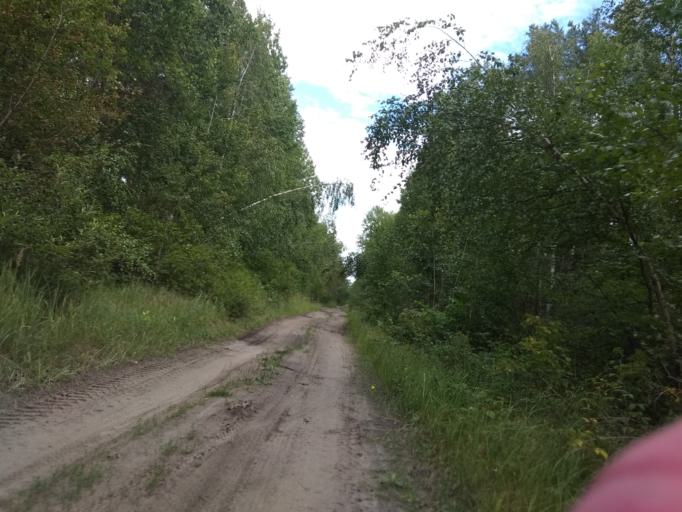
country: RU
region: Moskovskaya
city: Misheronskiy
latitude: 55.7091
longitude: 39.7308
